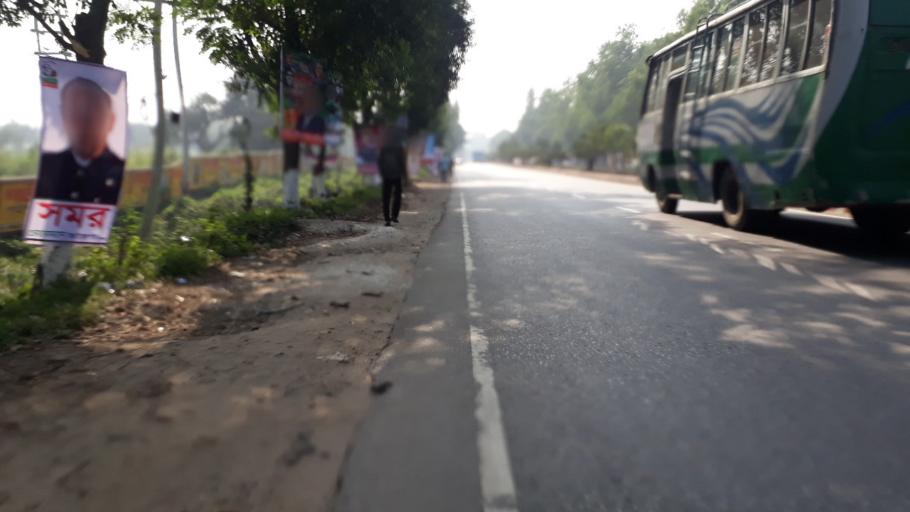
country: BD
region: Dhaka
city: Tungi
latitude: 23.8783
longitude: 90.2733
